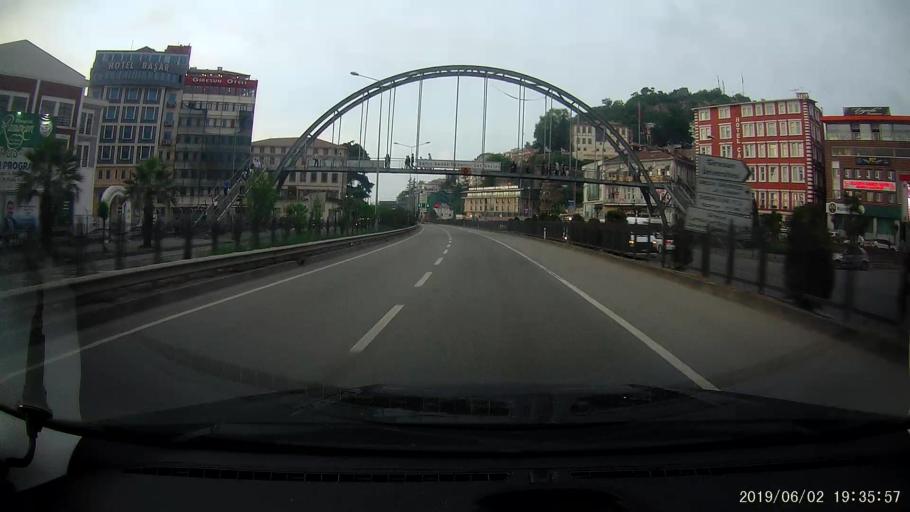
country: TR
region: Giresun
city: Giresun
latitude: 40.9183
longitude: 38.3839
